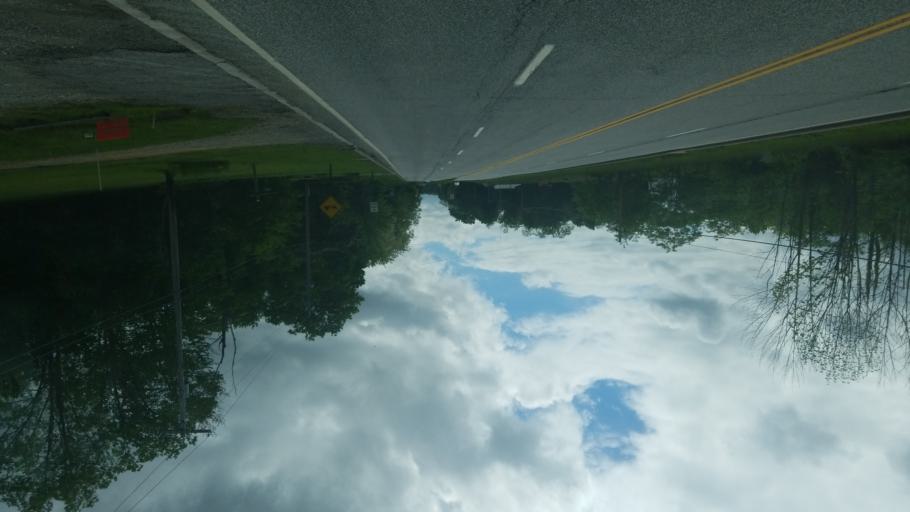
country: US
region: Ohio
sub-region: Portage County
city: Garrettsville
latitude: 41.3705
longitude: -81.0696
